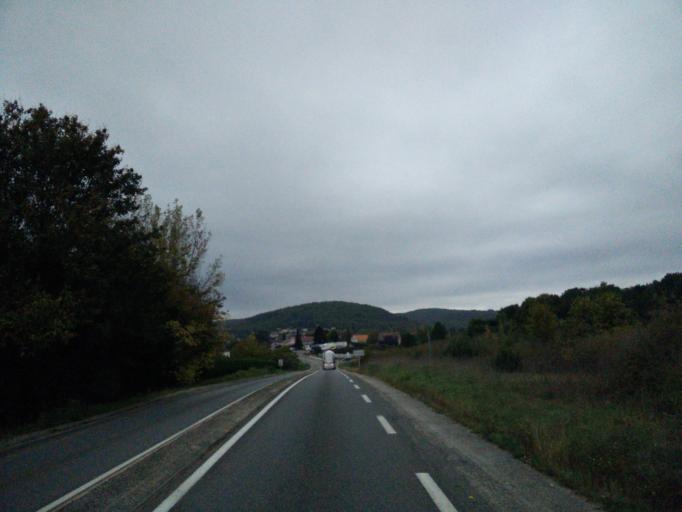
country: FR
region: Midi-Pyrenees
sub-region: Departement du Lot
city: Pradines
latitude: 44.5018
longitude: 1.3830
